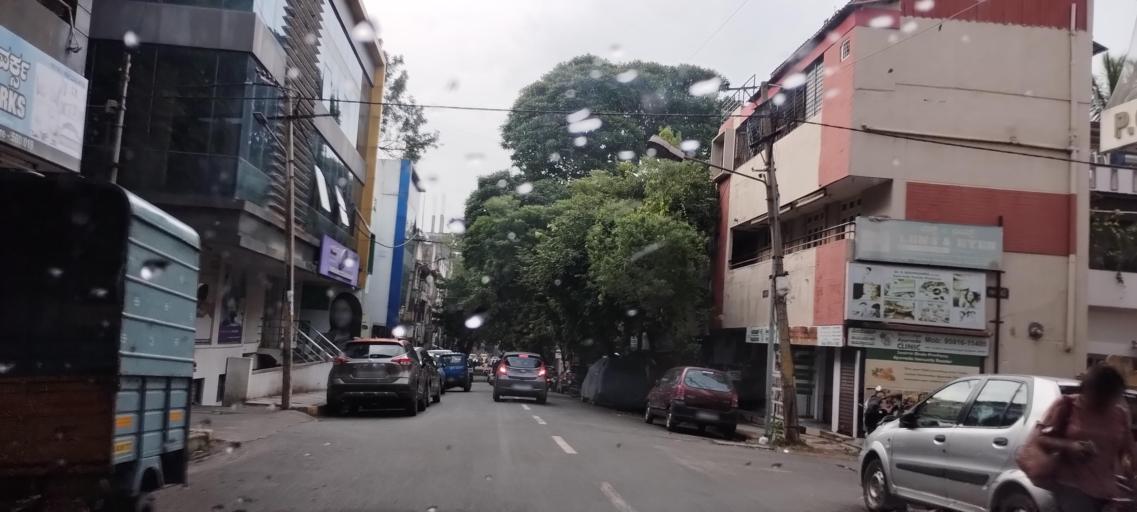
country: IN
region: Karnataka
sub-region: Bangalore Urban
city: Bangalore
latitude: 12.9420
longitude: 77.5643
